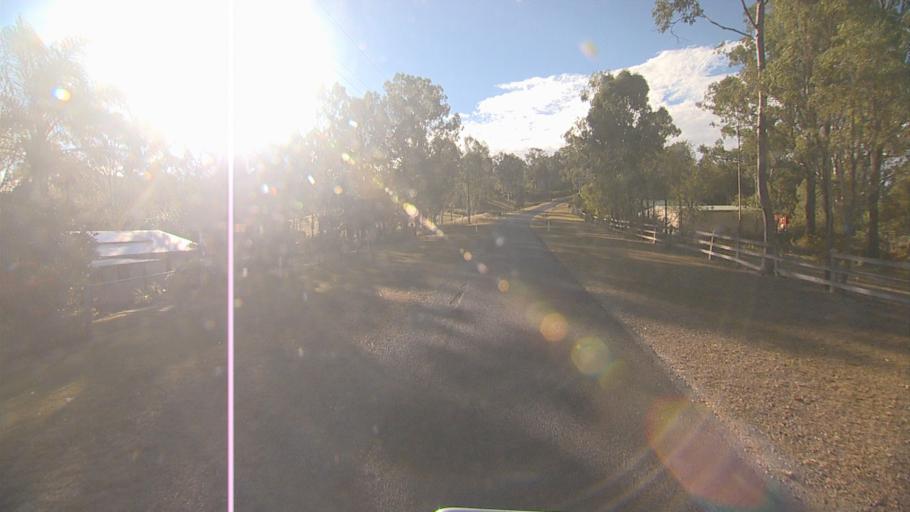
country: AU
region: Queensland
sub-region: Logan
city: Cedar Vale
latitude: -27.9242
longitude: 153.0665
